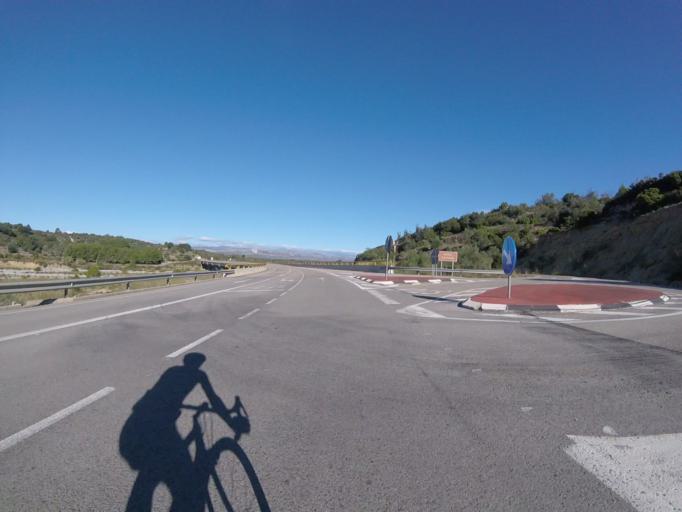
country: ES
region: Valencia
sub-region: Provincia de Castello
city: Cervera del Maestre
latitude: 40.4651
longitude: 0.2511
